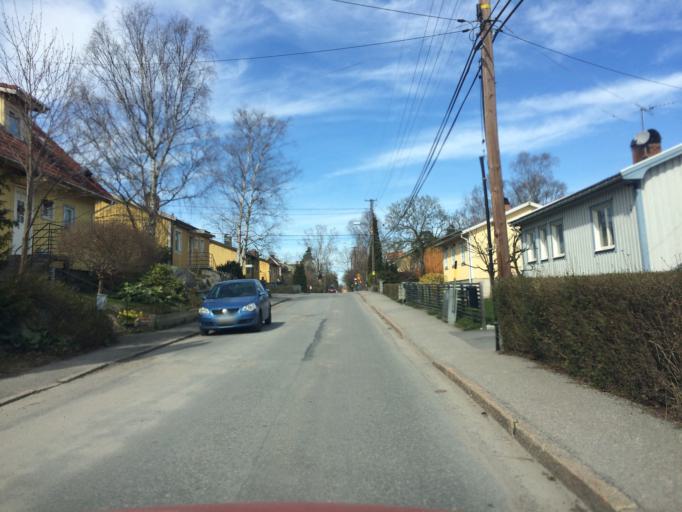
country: SE
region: Stockholm
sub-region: Huddinge Kommun
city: Huddinge
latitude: 59.2797
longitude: 17.9863
